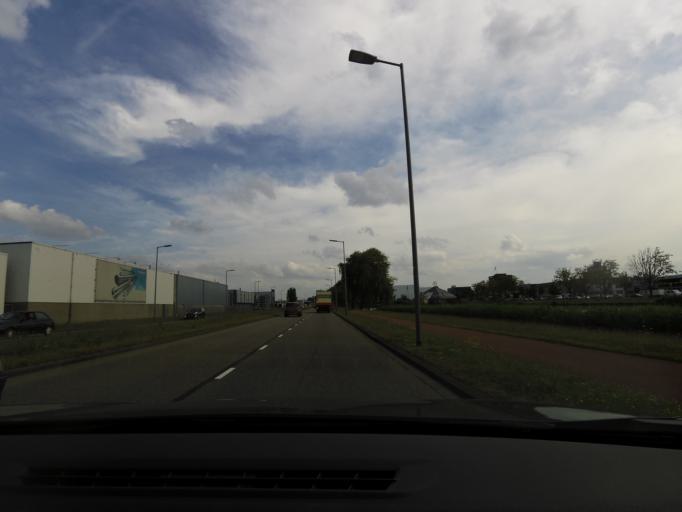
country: NL
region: South Holland
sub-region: Gemeente Schiedam
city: Schiedam
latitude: 51.9281
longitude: 4.4148
